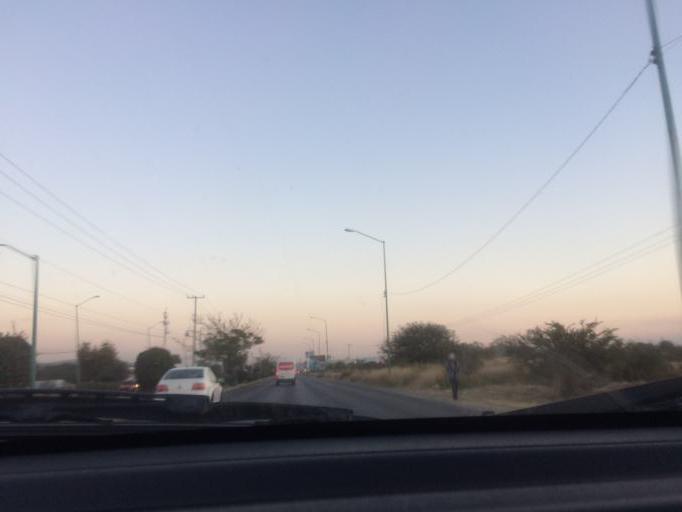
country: MX
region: Guanajuato
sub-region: Leon
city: Medina
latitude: 21.1553
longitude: -101.6400
